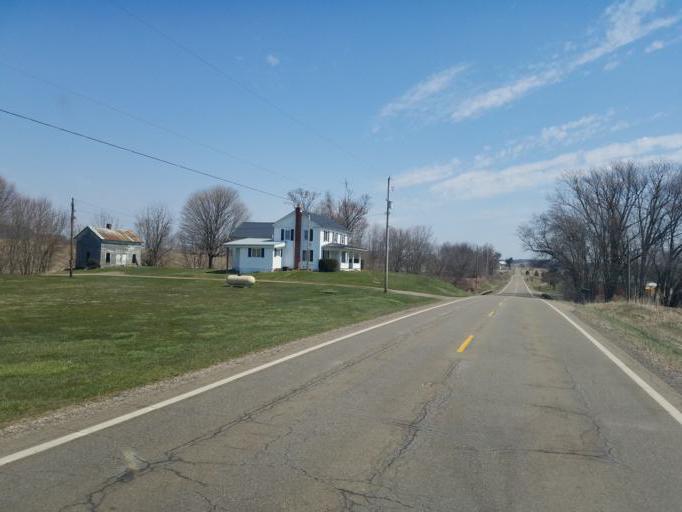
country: US
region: Ohio
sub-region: Ashland County
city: Loudonville
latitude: 40.6548
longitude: -82.1761
